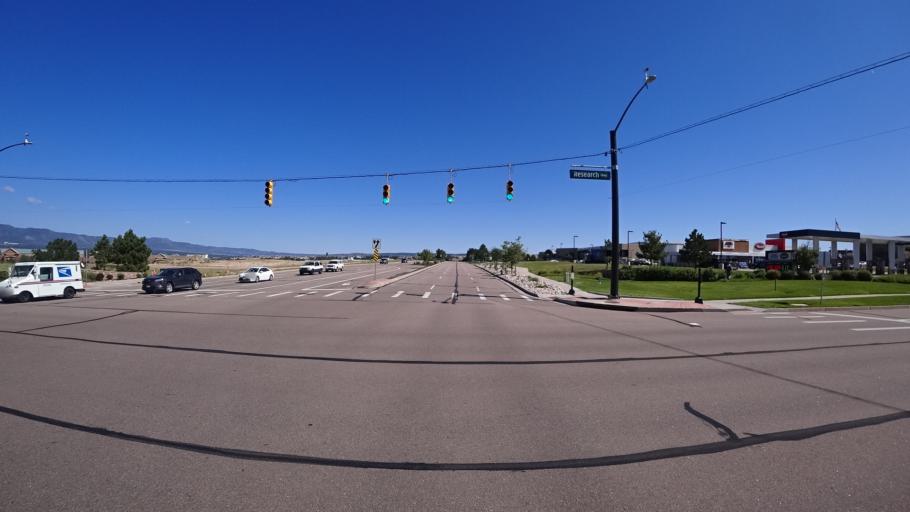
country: US
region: Colorado
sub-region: El Paso County
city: Air Force Academy
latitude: 38.9605
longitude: -104.7846
